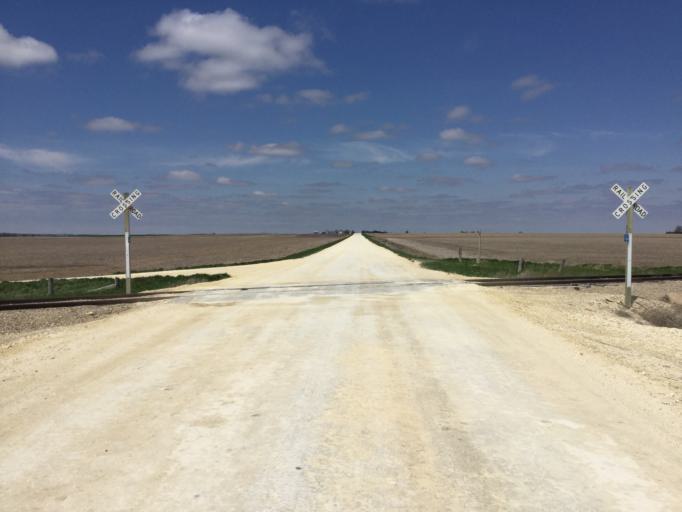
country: US
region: Kansas
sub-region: Osborne County
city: Osborne
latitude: 39.5133
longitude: -98.5068
